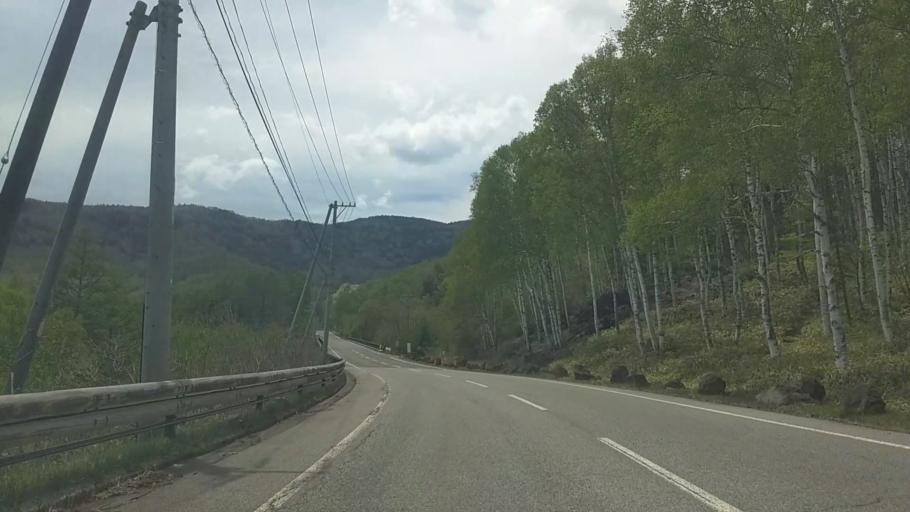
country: JP
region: Nagano
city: Saku
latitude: 36.0759
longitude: 138.3826
